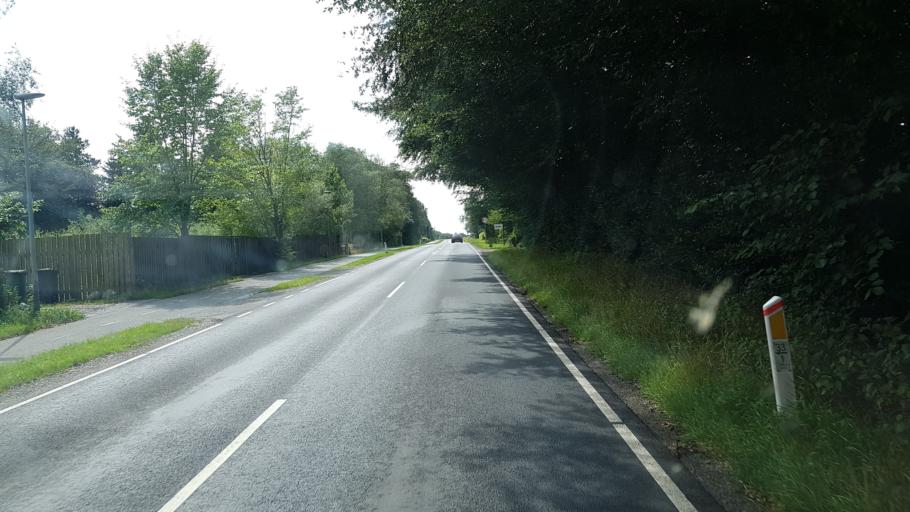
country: DK
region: South Denmark
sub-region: Vejen Kommune
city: Vejen
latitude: 55.5635
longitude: 9.1303
